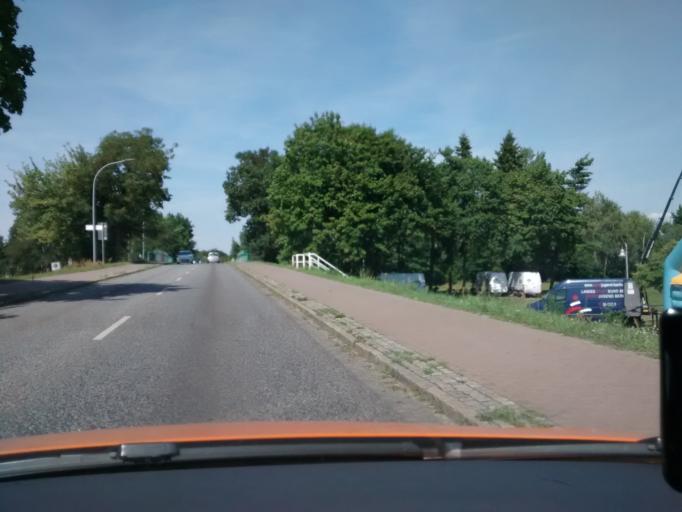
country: DE
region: Brandenburg
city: Hohen Neuendorf
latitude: 52.6731
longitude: 13.2801
